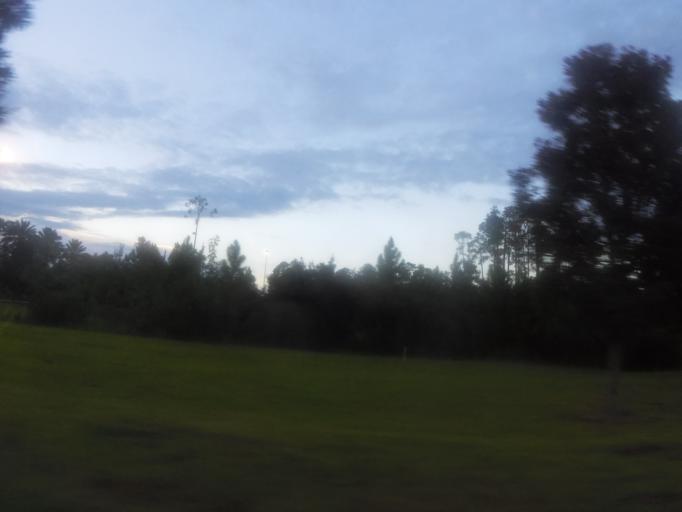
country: US
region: Florida
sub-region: Saint Johns County
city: Palm Valley
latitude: 30.1150
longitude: -81.4174
